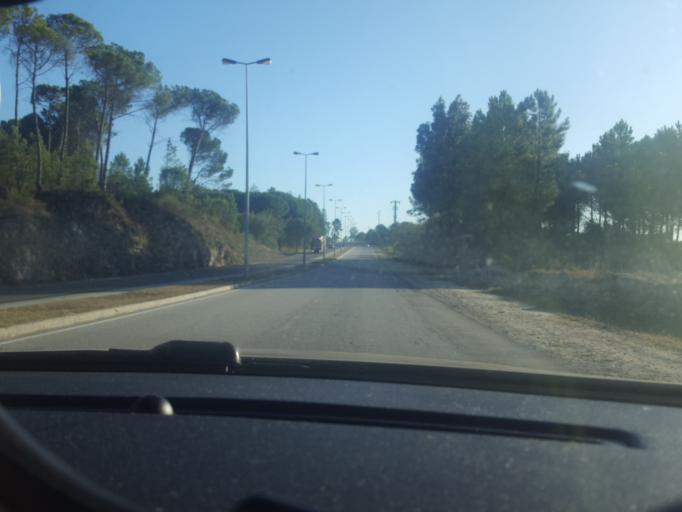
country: PT
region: Viseu
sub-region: Nelas
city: Nelas
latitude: 40.5325
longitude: -7.8636
